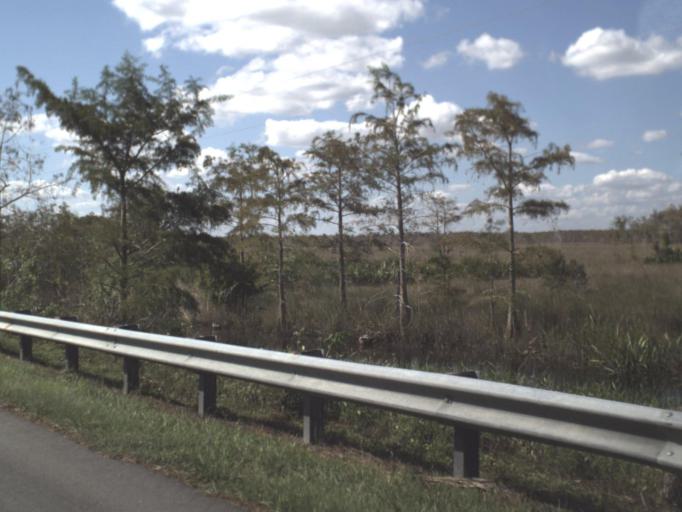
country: US
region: Florida
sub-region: Collier County
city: Immokalee
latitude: 25.8614
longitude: -81.0780
